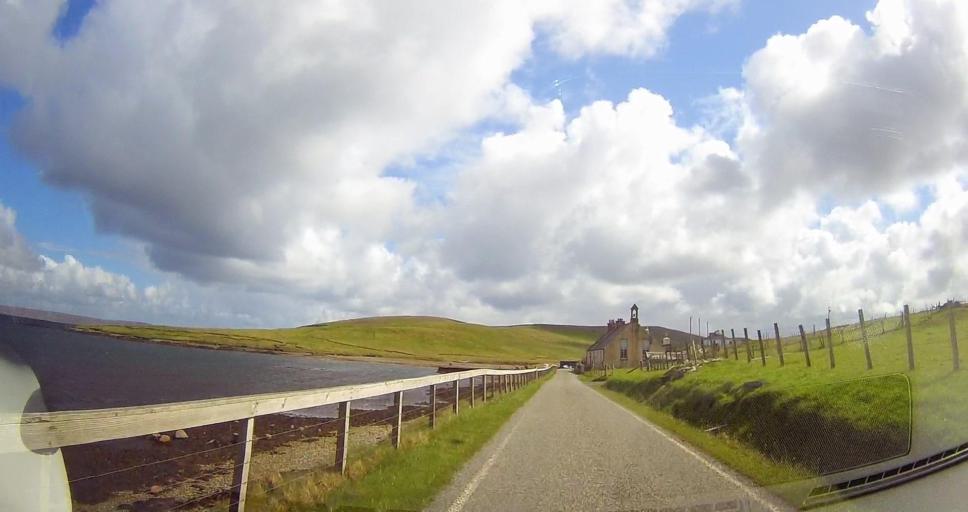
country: GB
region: Scotland
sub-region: Shetland Islands
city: Lerwick
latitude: 60.5794
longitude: -1.3330
